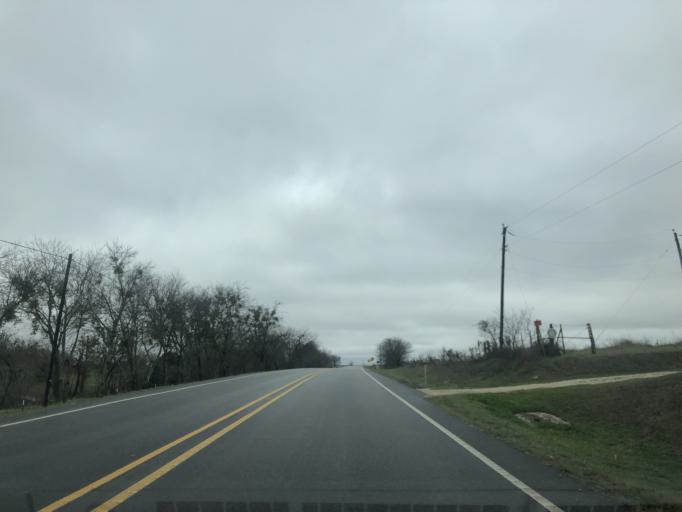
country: US
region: Texas
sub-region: Williamson County
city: Hutto
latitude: 30.6194
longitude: -97.5436
